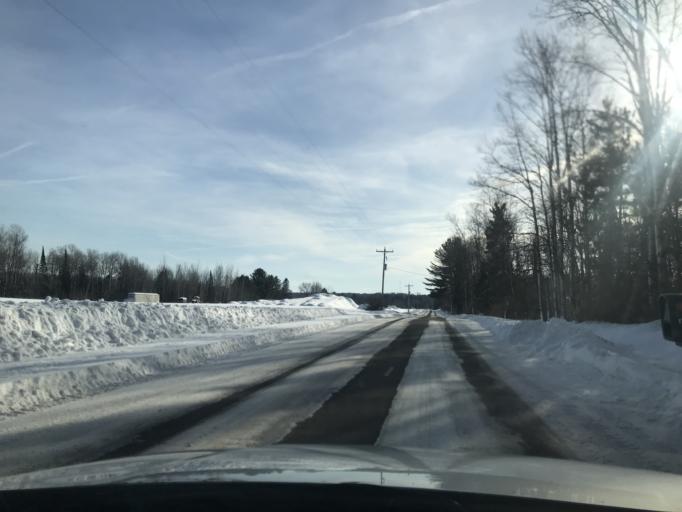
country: US
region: Wisconsin
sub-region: Menominee County
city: Legend Lake
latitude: 45.3123
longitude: -88.5218
